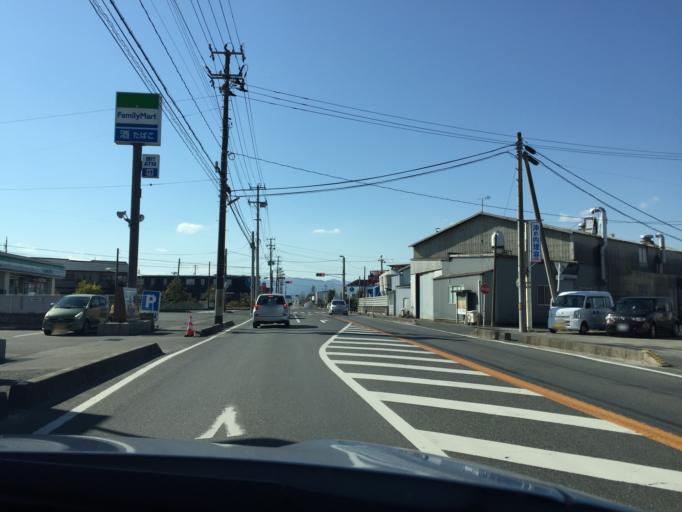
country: JP
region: Miyagi
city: Marumori
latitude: 37.8047
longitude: 140.9320
